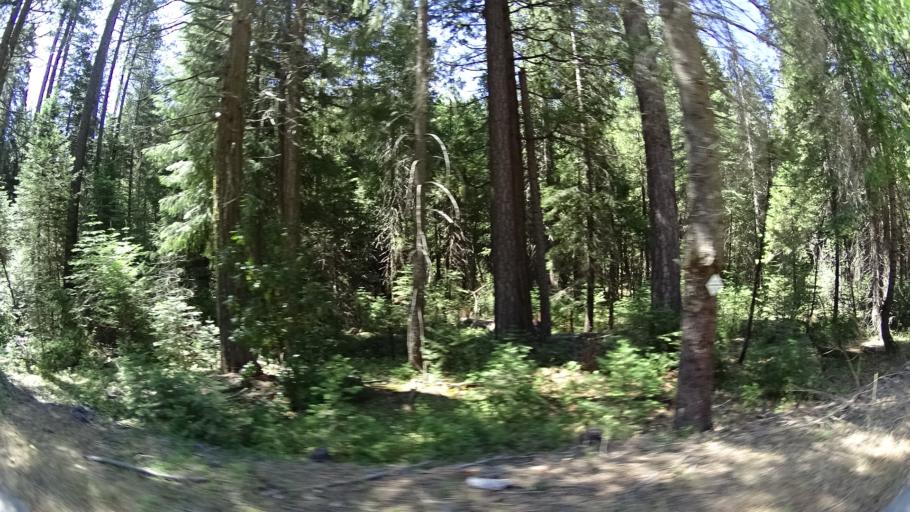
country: US
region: California
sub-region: Amador County
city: Pioneer
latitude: 38.4299
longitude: -120.4551
